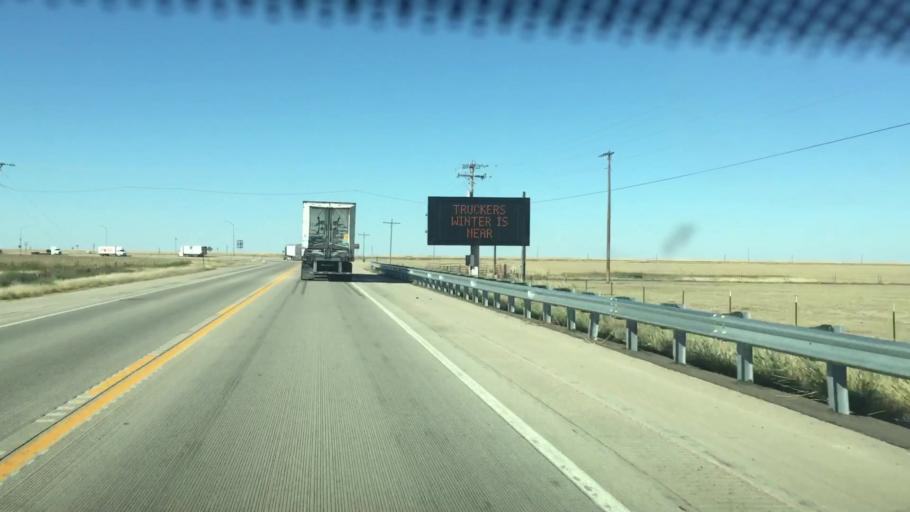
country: US
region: Colorado
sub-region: Kiowa County
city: Eads
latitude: 38.4685
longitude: -102.7307
